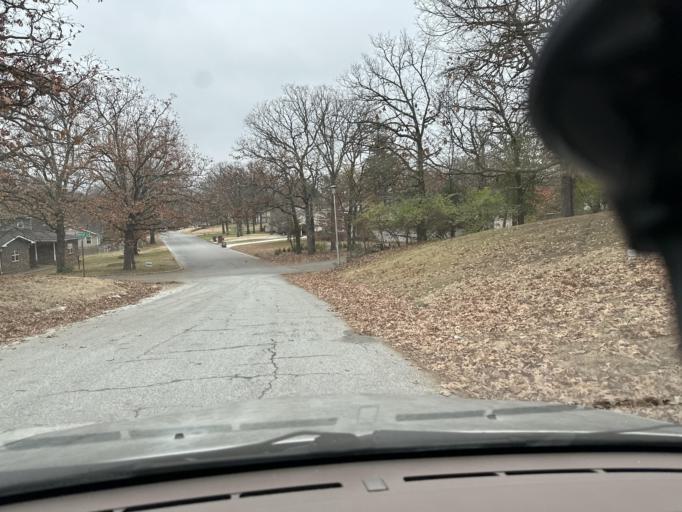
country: US
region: Arkansas
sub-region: Washington County
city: Johnson
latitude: 36.1027
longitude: -94.1419
